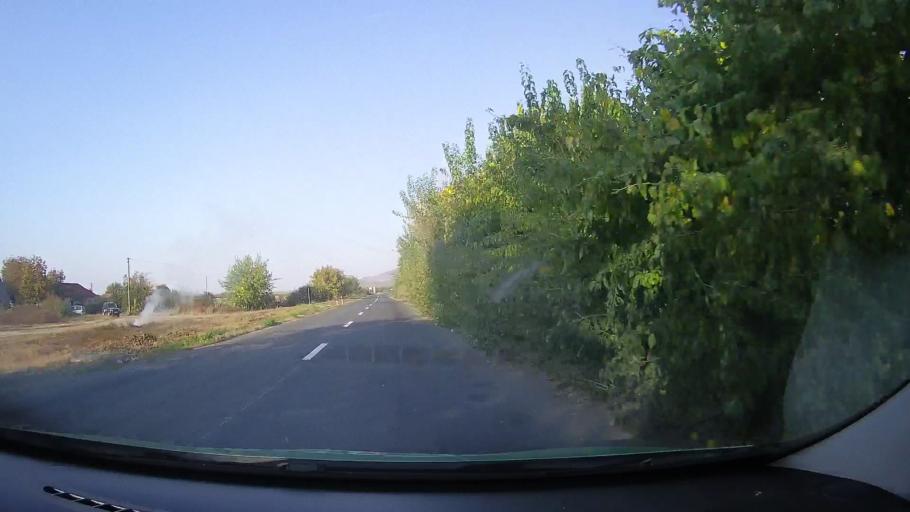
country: RO
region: Arad
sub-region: Comuna Covasint
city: Covasint
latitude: 46.2101
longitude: 21.6111
